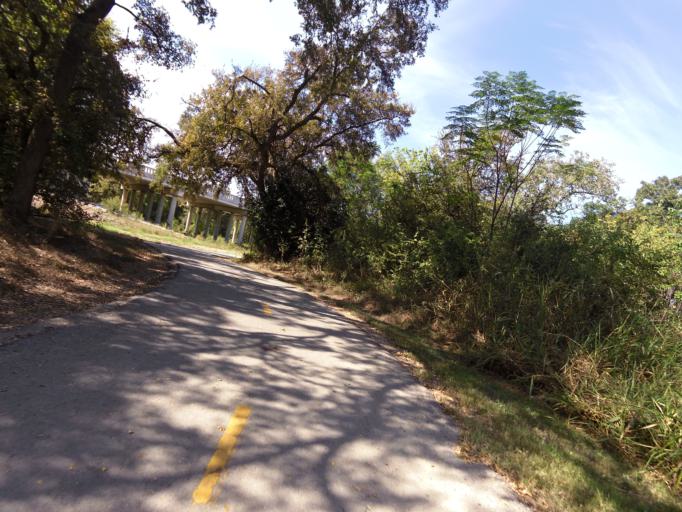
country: US
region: Texas
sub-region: Bexar County
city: Terrell Hills
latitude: 29.4248
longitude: -98.4313
